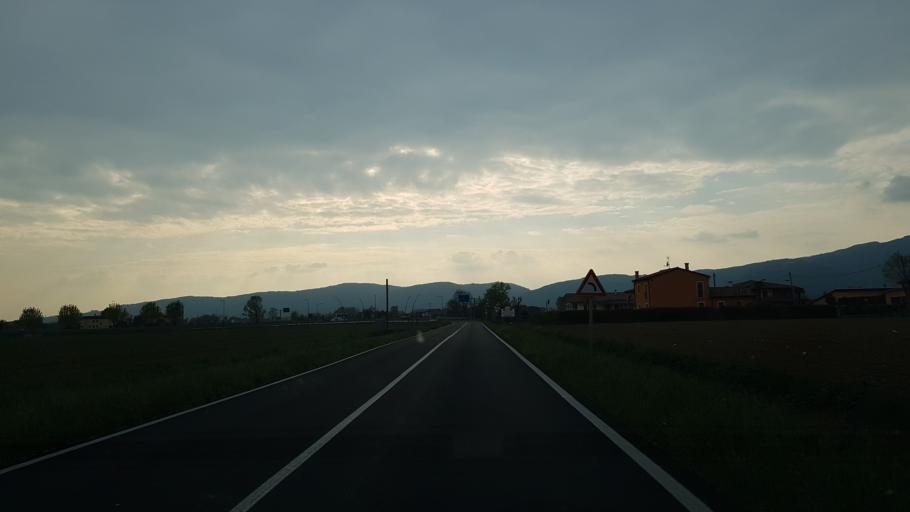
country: IT
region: Veneto
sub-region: Provincia di Vicenza
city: Ponte di Barbarano
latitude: 45.3861
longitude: 11.5687
